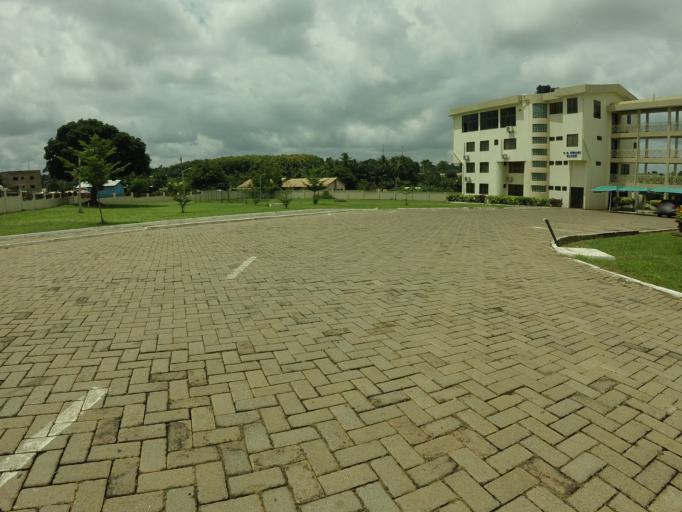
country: GH
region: Volta
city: Ho
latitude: 6.5917
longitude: 0.4701
